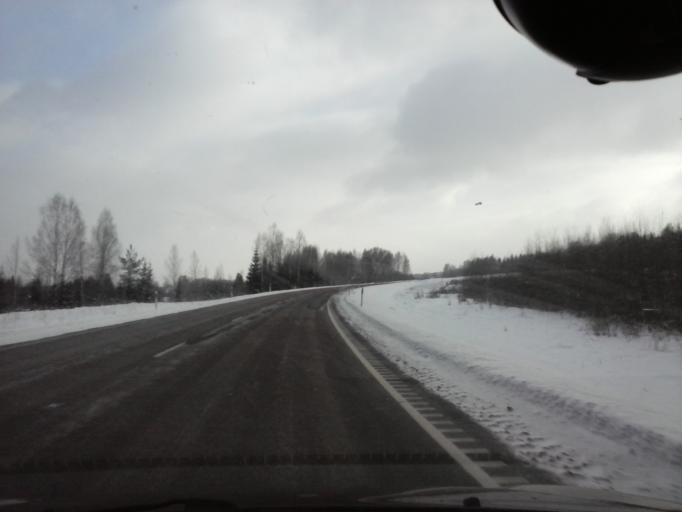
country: EE
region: Viljandimaa
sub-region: Viljandi linn
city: Viljandi
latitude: 58.3485
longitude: 25.4645
